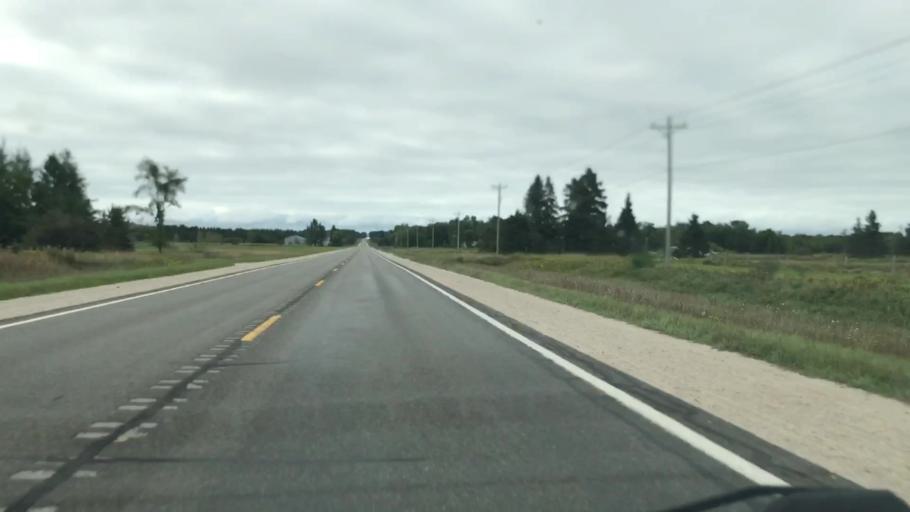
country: US
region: Michigan
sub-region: Luce County
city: Newberry
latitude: 46.1434
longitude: -85.5713
